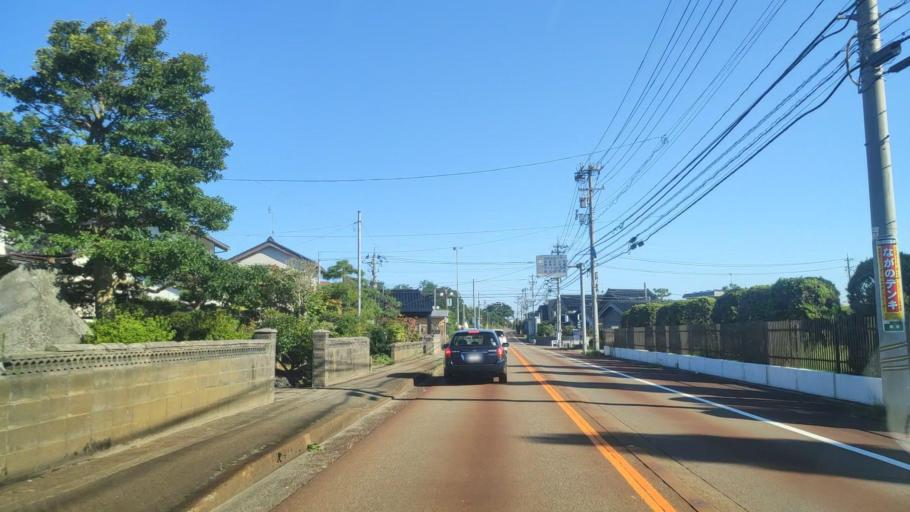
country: JP
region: Ishikawa
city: Hakui
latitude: 36.8561
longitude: 136.7695
